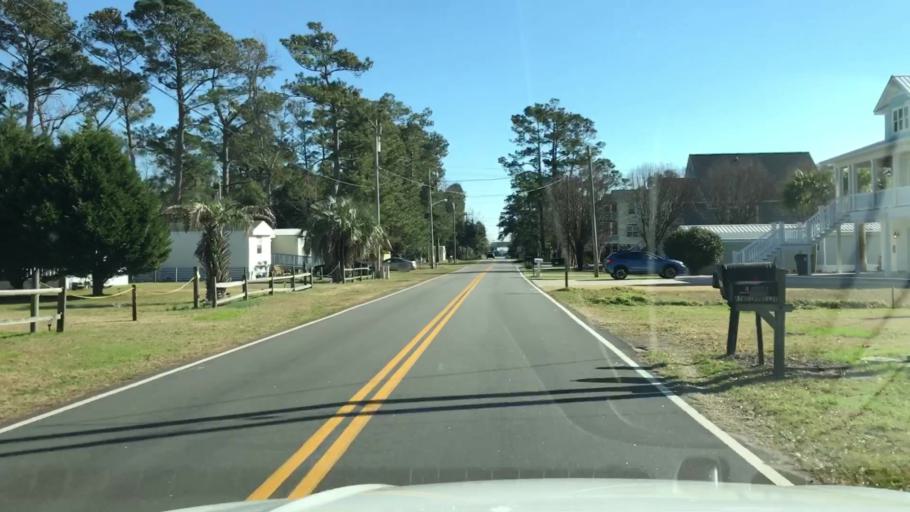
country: US
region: South Carolina
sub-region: Horry County
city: Garden City
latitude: 33.5902
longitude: -78.9966
